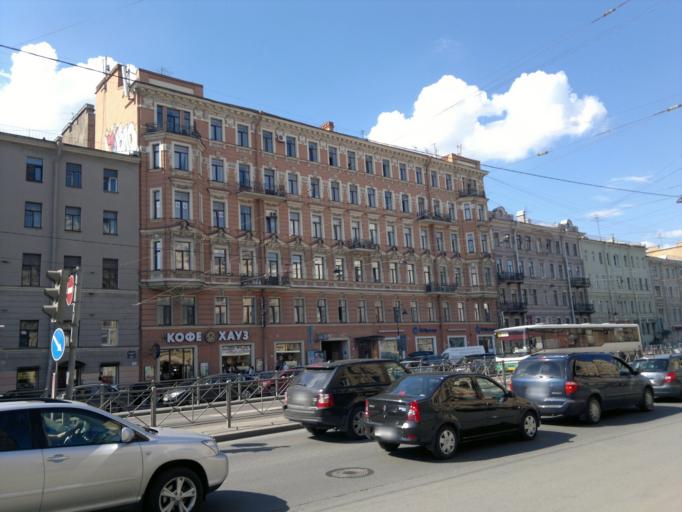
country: RU
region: St.-Petersburg
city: Centralniy
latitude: 59.9238
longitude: 30.3567
